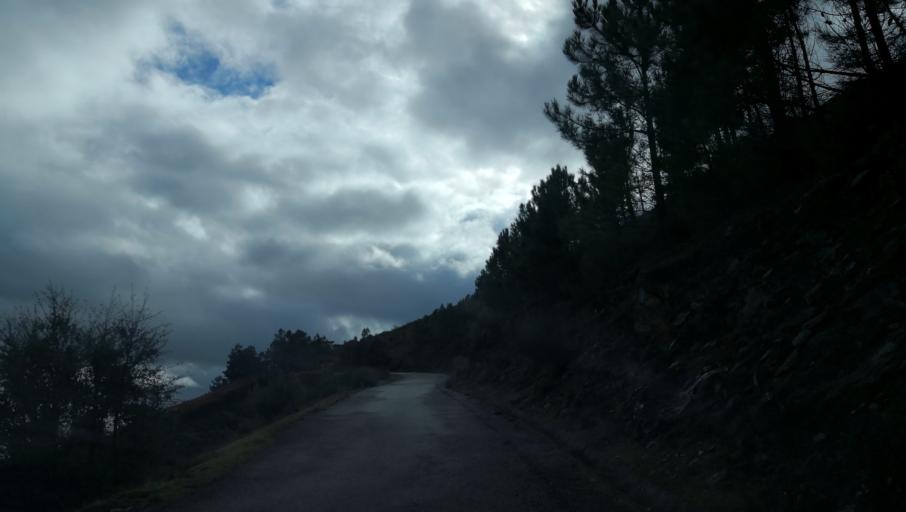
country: PT
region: Vila Real
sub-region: Sabrosa
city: Vilela
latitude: 41.1990
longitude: -7.5777
